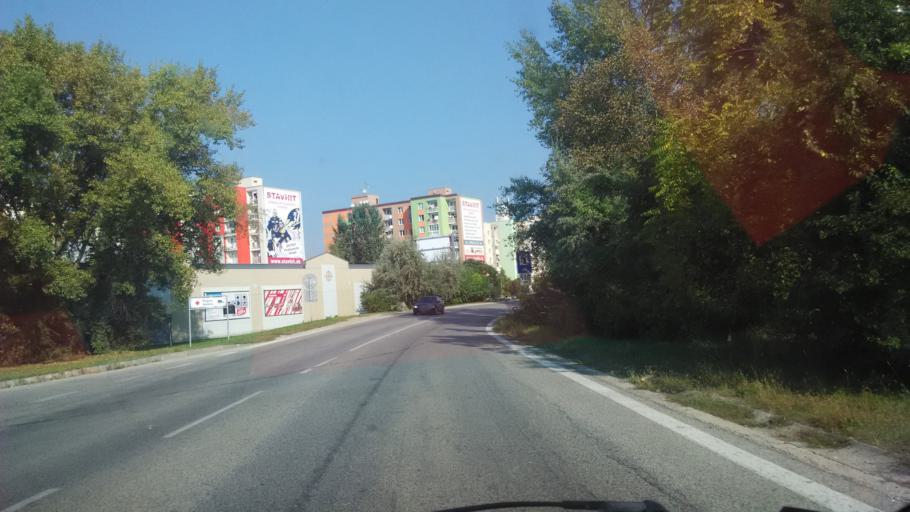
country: SK
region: Trnavsky
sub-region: Okres Trnava
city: Piestany
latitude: 48.5796
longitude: 17.8134
